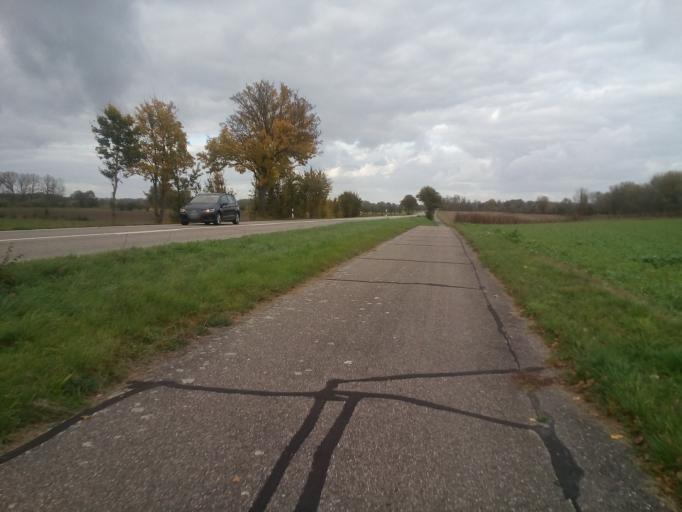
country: DE
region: Baden-Wuerttemberg
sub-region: Karlsruhe Region
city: Hugelsheim
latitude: 48.7882
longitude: 8.0804
